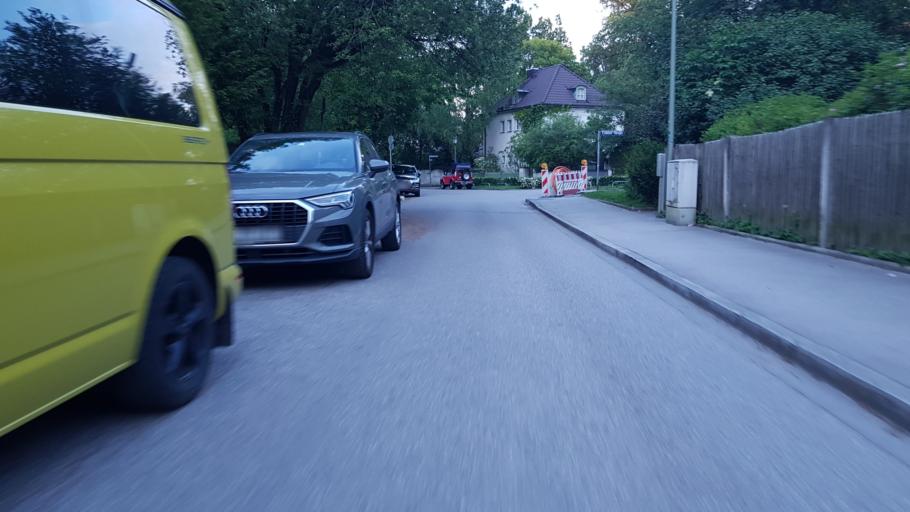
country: DE
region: Bavaria
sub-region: Upper Bavaria
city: Pasing
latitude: 48.1543
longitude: 11.5037
